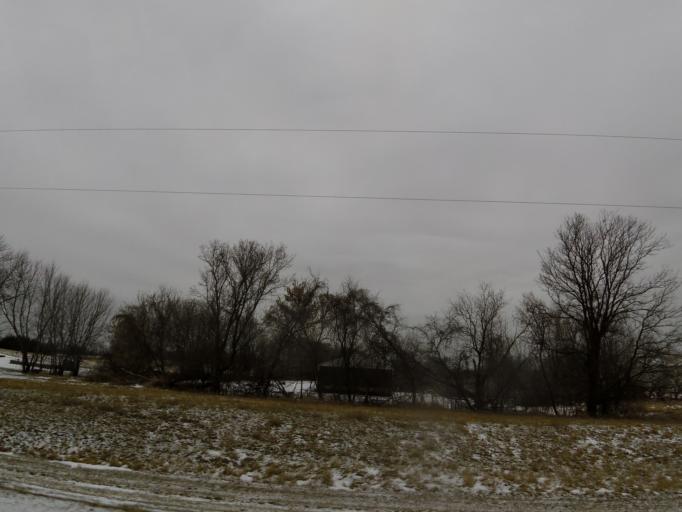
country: US
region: Minnesota
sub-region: Wright County
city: Montrose
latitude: 45.0586
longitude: -93.8591
